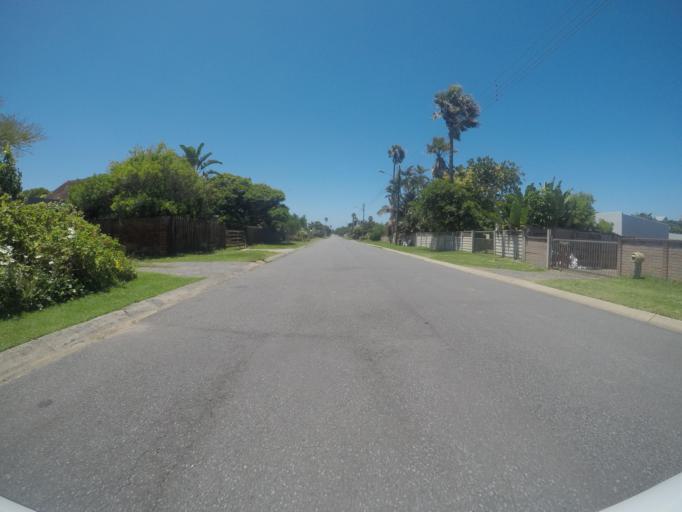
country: ZA
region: Eastern Cape
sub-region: Buffalo City Metropolitan Municipality
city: East London
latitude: -32.9490
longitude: 28.0150
